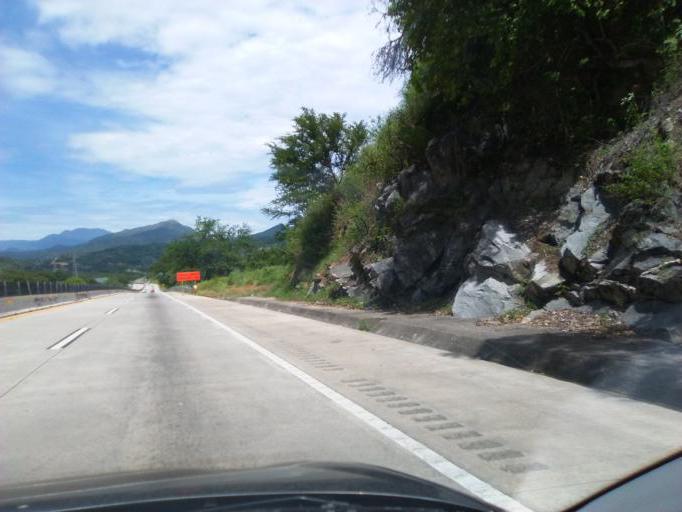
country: MX
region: Guerrero
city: Tierra Colorada
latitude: 17.1526
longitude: -99.5540
